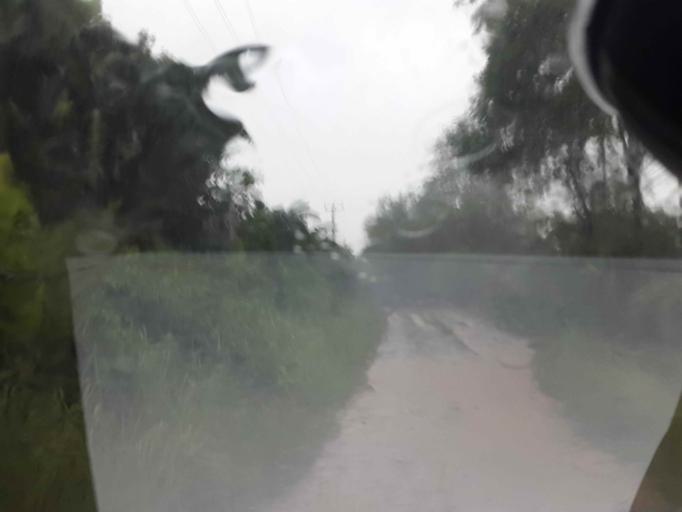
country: ID
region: Lampung
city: Kedaton
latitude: -5.3921
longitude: 105.3293
